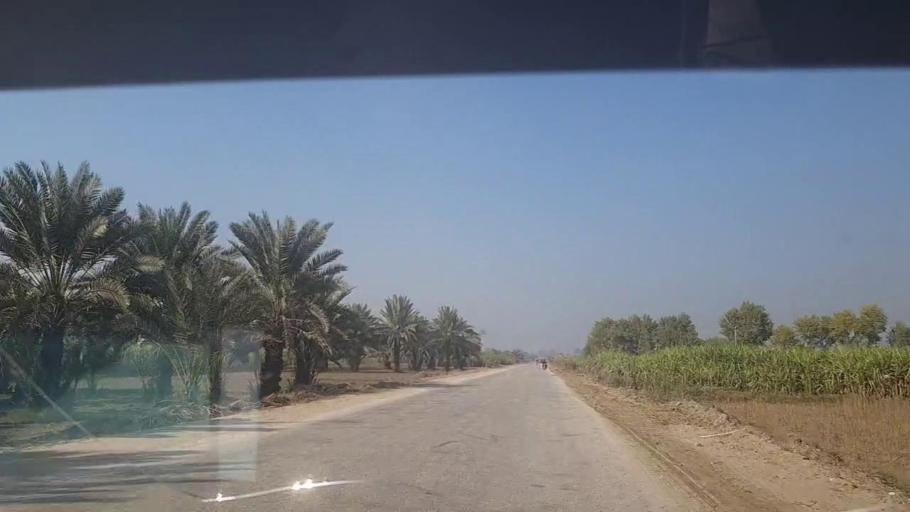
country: PK
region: Sindh
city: Kot Diji
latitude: 27.4215
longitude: 68.6601
